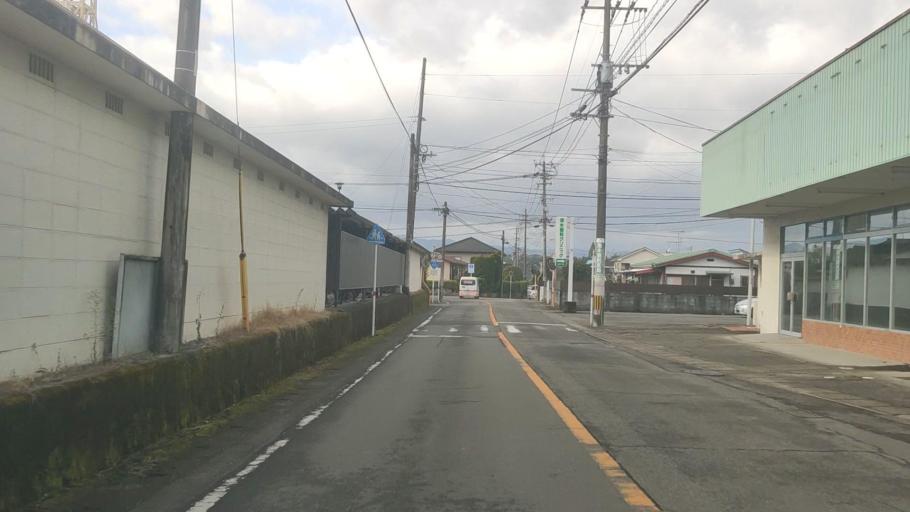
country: JP
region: Kumamoto
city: Hitoyoshi
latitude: 32.2224
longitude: 130.7723
